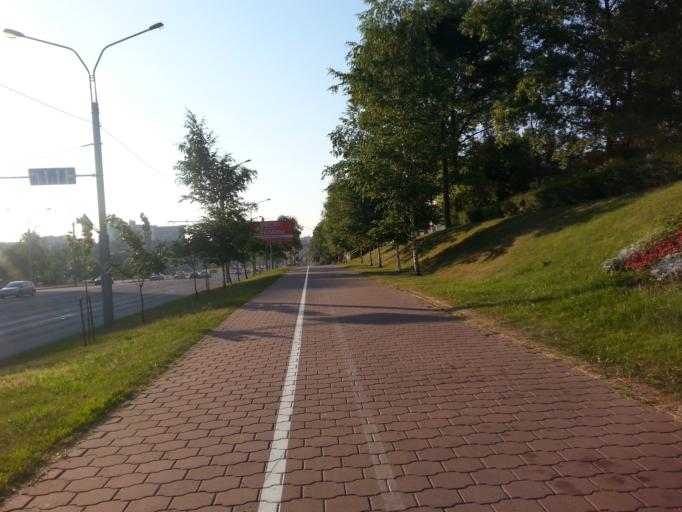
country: BY
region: Minsk
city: Vyaliki Trastsyanets
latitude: 53.8642
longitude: 27.6652
